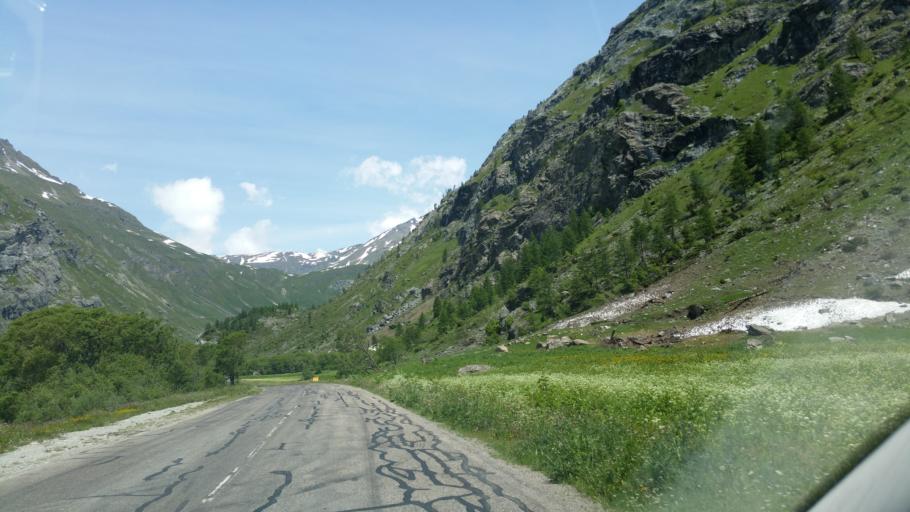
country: FR
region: Rhone-Alpes
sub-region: Departement de la Savoie
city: Val-d'Isere
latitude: 45.3460
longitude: 7.0293
